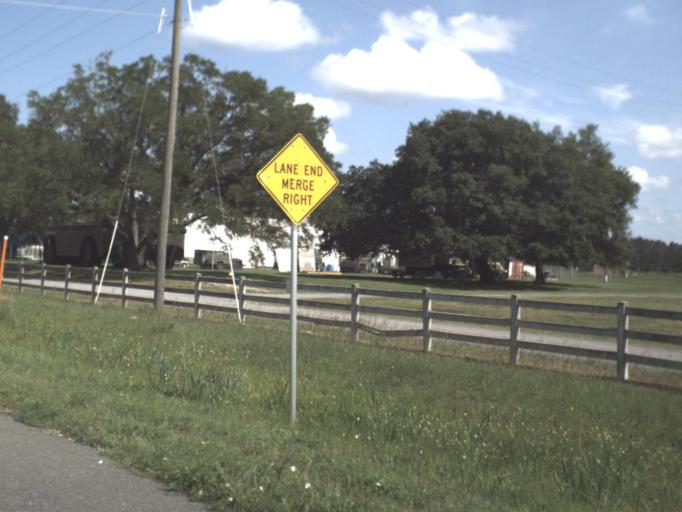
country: US
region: Florida
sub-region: Clay County
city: Green Cove Springs
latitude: 29.9806
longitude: -81.6543
